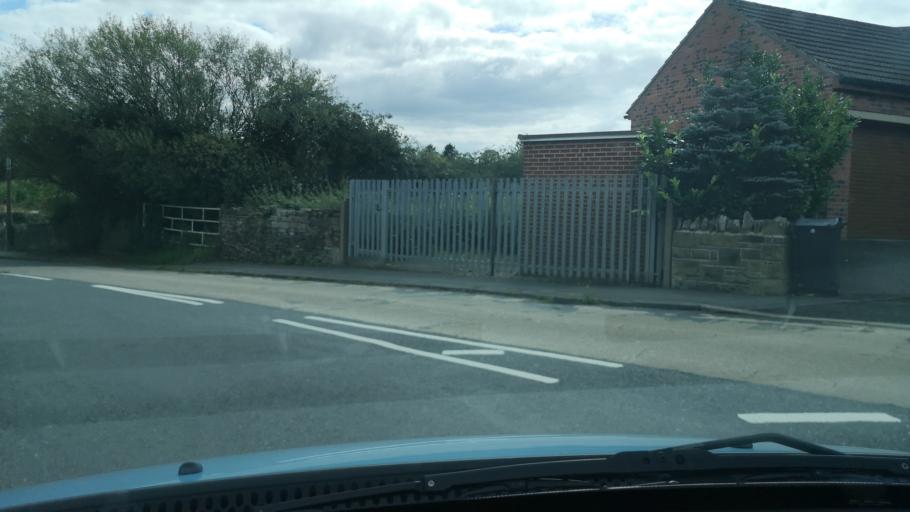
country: GB
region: England
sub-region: Kirklees
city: Mirfield
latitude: 53.6618
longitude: -1.7042
